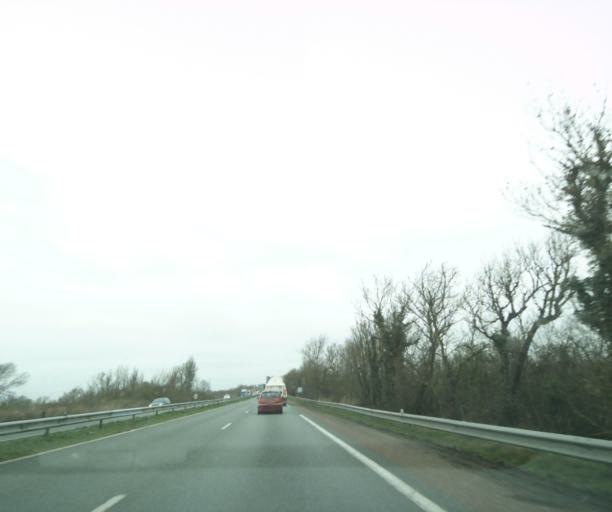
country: FR
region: Poitou-Charentes
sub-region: Departement de la Charente-Maritime
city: Angoulins
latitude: 46.1160
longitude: -1.1054
